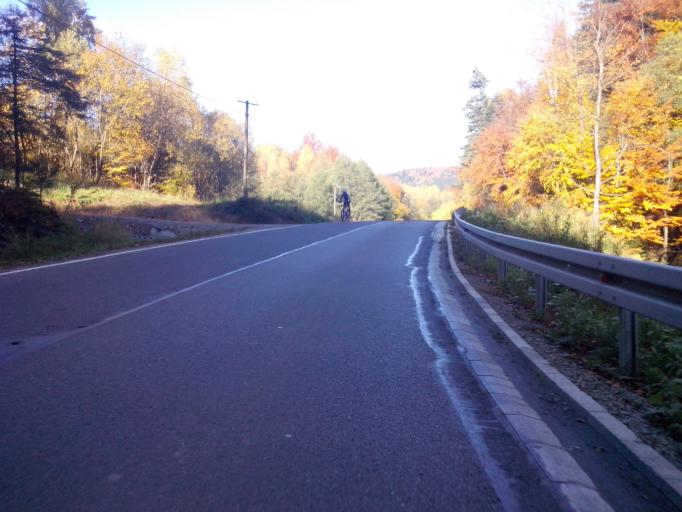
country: PL
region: Subcarpathian Voivodeship
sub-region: Powiat krosnienski
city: Korczyna
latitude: 49.7583
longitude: 21.7938
